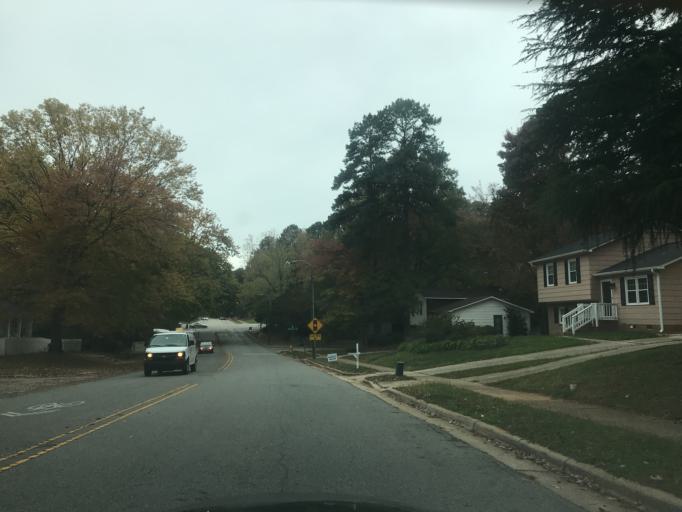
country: US
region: North Carolina
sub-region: Wake County
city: West Raleigh
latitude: 35.8836
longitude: -78.6586
